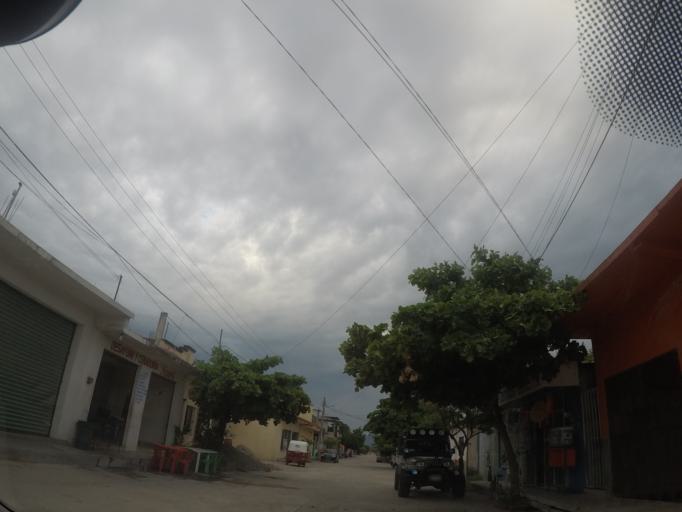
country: MX
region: Oaxaca
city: Chahuite
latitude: 16.2892
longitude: -94.1946
